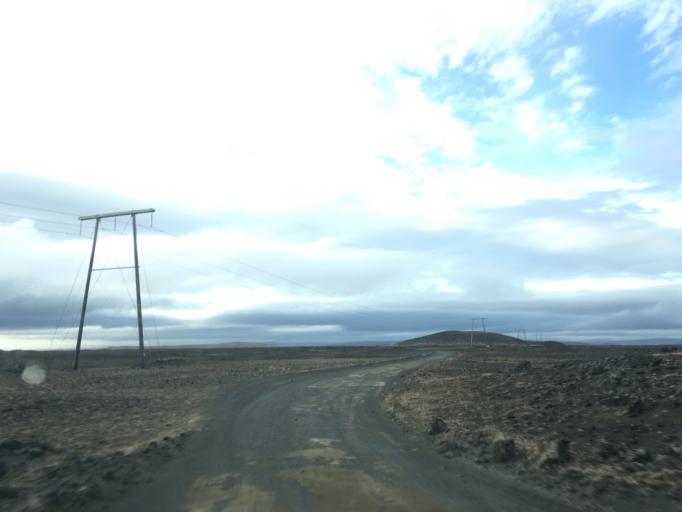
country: IS
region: South
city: Vestmannaeyjar
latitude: 64.1153
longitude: -19.1123
